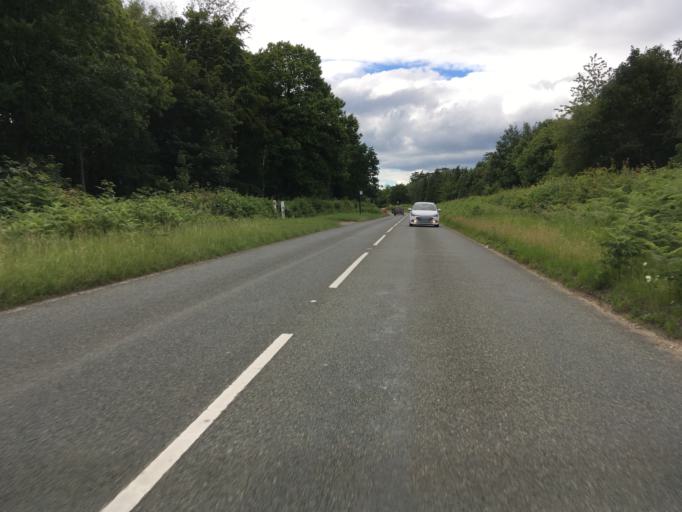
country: GB
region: England
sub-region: Oxfordshire
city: Boars Hill
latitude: 51.7126
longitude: -1.2653
